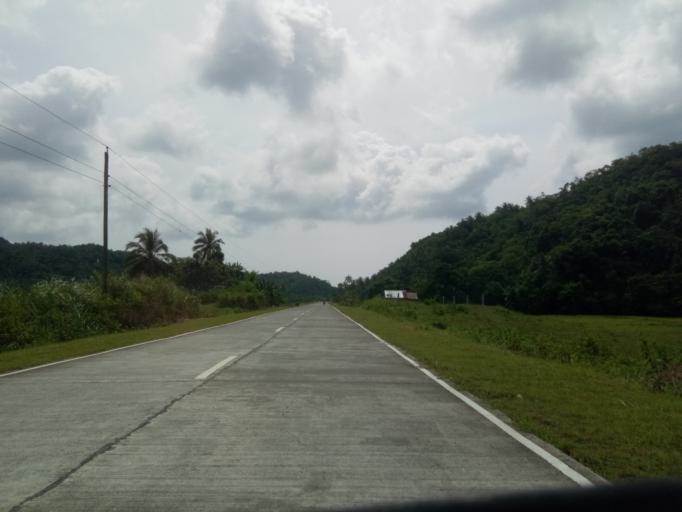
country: PH
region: Caraga
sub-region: Province of Surigao del Norte
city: Pilar
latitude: 9.8930
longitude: 126.0775
